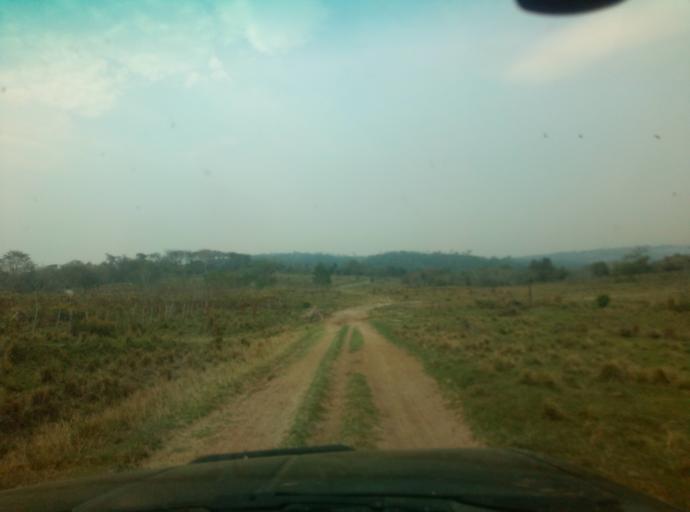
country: PY
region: Caaguazu
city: San Joaquin
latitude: -25.1023
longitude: -56.1243
